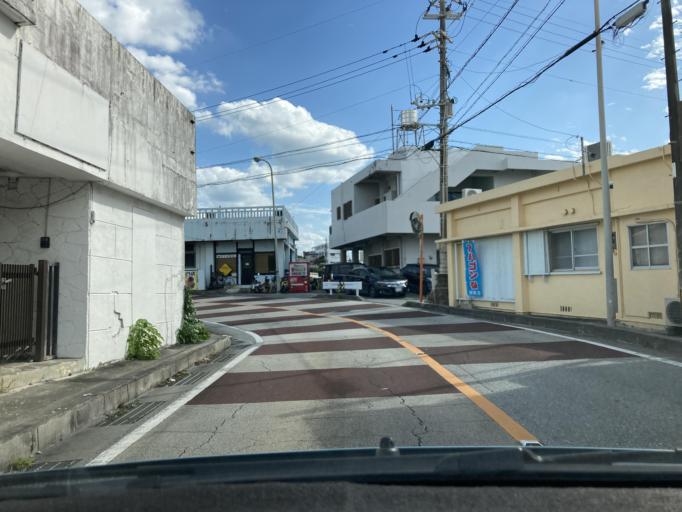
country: JP
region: Okinawa
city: Chatan
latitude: 26.3146
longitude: 127.7691
